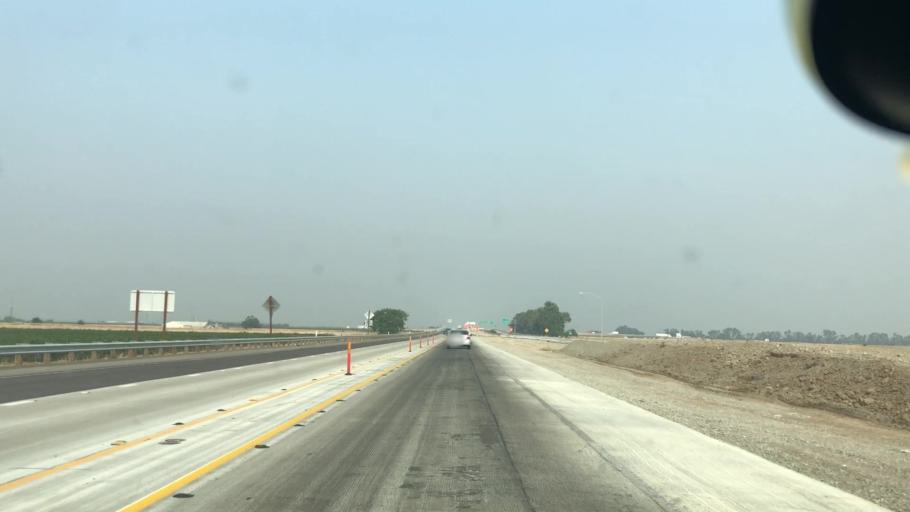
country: US
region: California
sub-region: San Joaquin County
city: Tracy
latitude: 37.6379
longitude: -121.3575
